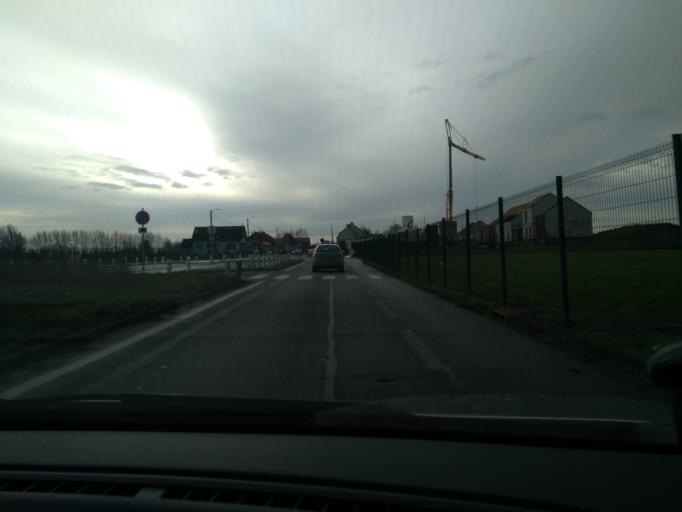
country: BE
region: Wallonia
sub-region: Province du Hainaut
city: Quevy-le-Petit
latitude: 50.3417
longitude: 3.9710
